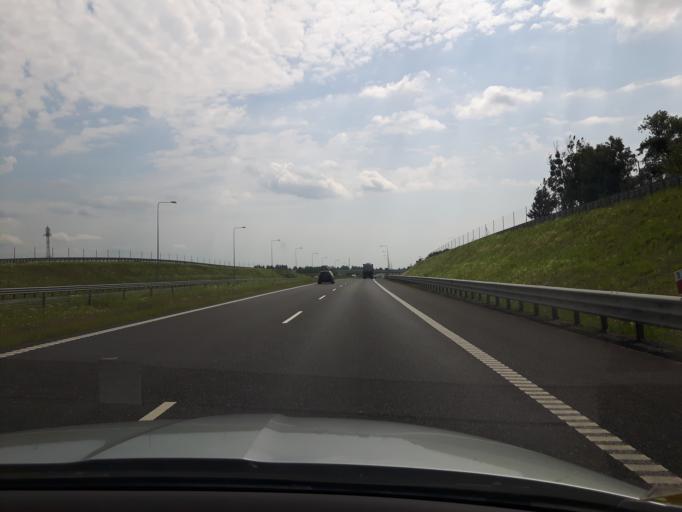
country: PL
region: Warmian-Masurian Voivodeship
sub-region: Powiat olsztynski
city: Olsztynek
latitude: 53.5050
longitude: 20.3089
